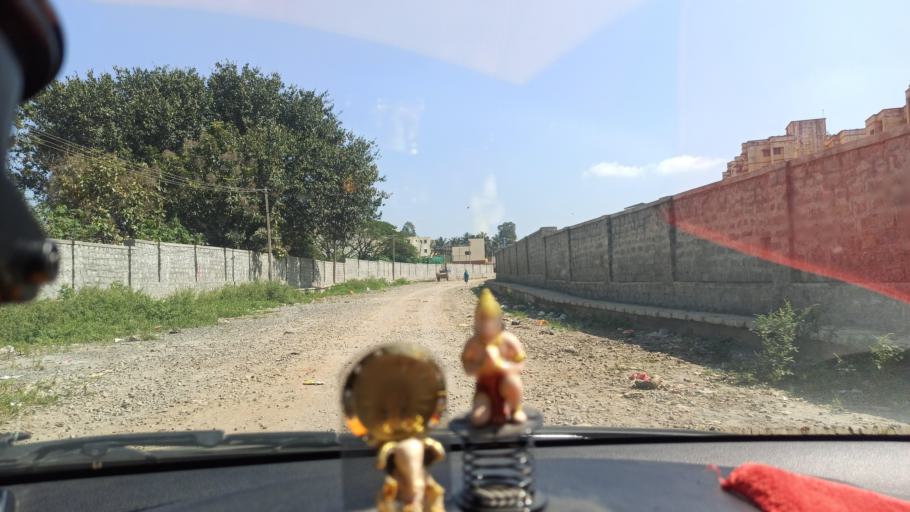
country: IN
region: Karnataka
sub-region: Bangalore Urban
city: Bangalore
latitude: 12.9612
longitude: 77.6971
